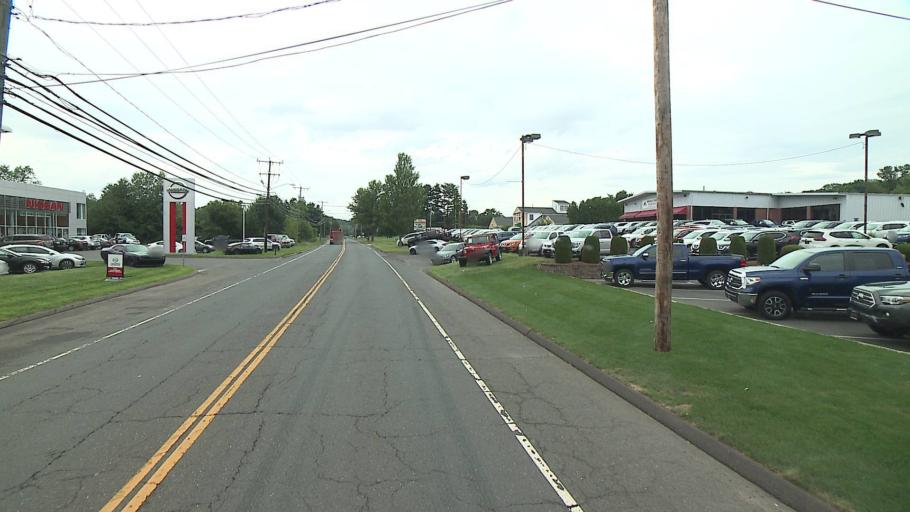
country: US
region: Connecticut
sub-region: Middlesex County
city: Cromwell
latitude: 41.5904
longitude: -72.6757
